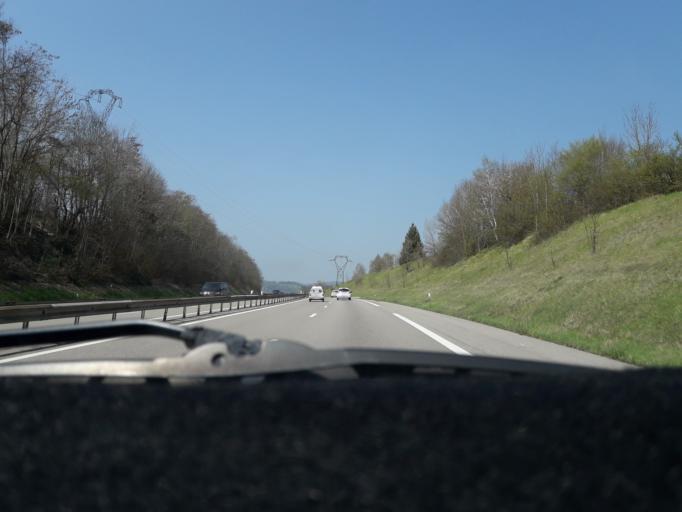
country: FR
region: Rhone-Alpes
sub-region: Departement de l'Isere
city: Chabons
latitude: 45.4239
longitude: 5.4443
